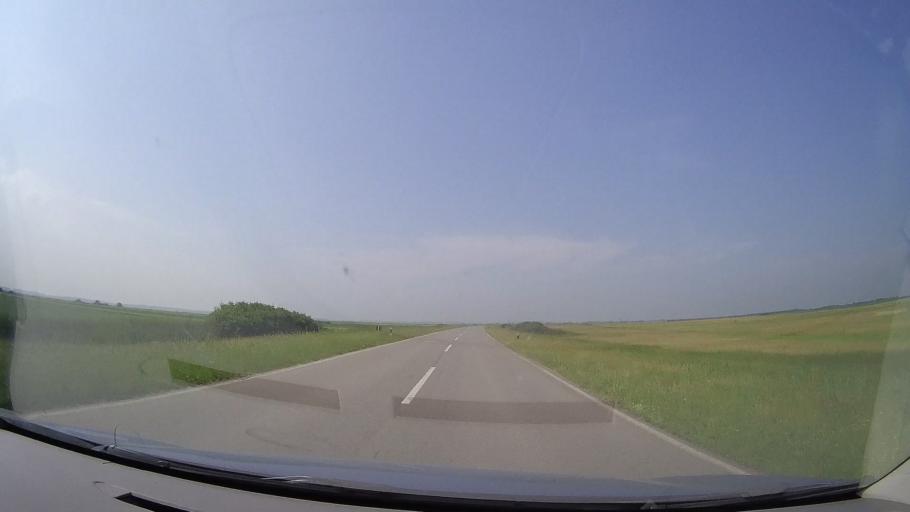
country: RS
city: Jasa Tomic
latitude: 45.4177
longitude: 20.8335
